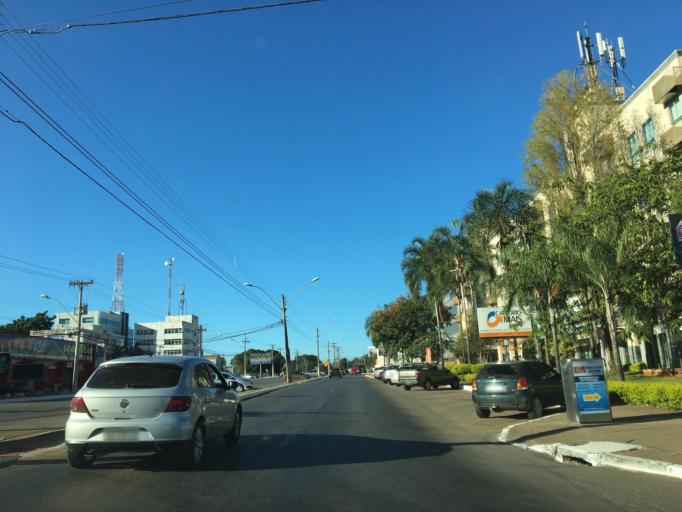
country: BR
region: Federal District
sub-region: Brasilia
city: Brasilia
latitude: -15.7976
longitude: -47.9496
